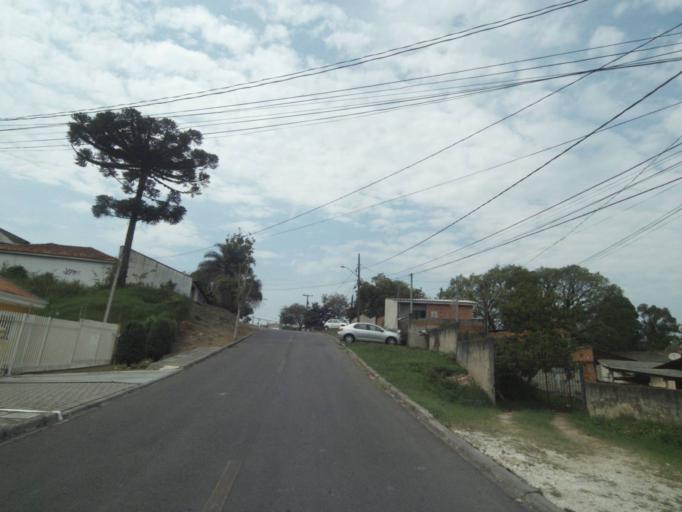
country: BR
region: Parana
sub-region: Pinhais
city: Pinhais
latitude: -25.4236
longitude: -49.2088
